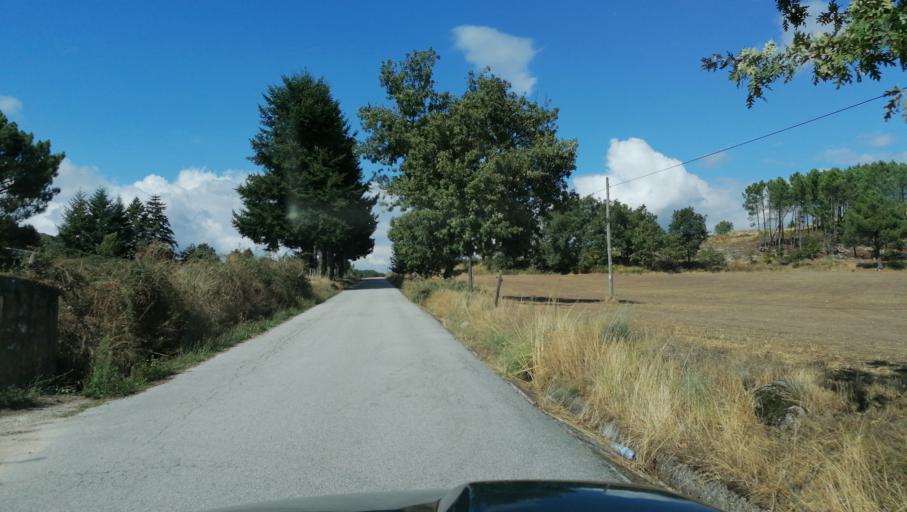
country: PT
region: Vila Real
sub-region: Vila Pouca de Aguiar
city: Vila Pouca de Aguiar
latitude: 41.5579
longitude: -7.6428
